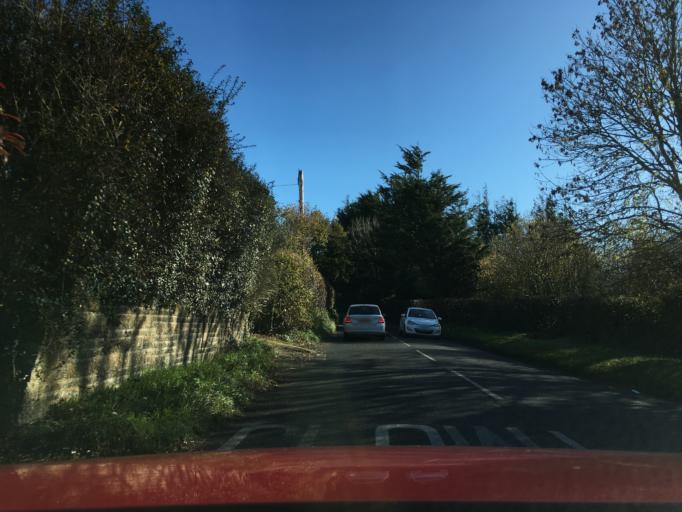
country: GB
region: England
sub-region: Somerset
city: Yeovil
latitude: 50.9614
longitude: -2.6686
